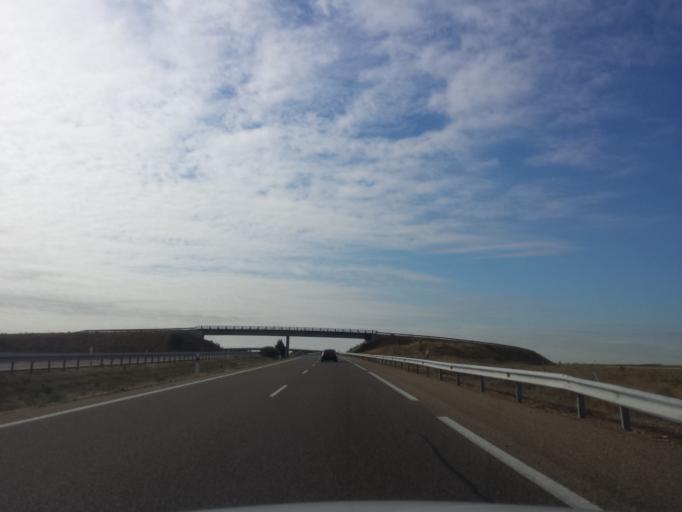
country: ES
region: Castille and Leon
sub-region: Provincia de Leon
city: Onzonilla
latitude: 42.4825
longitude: -5.5971
